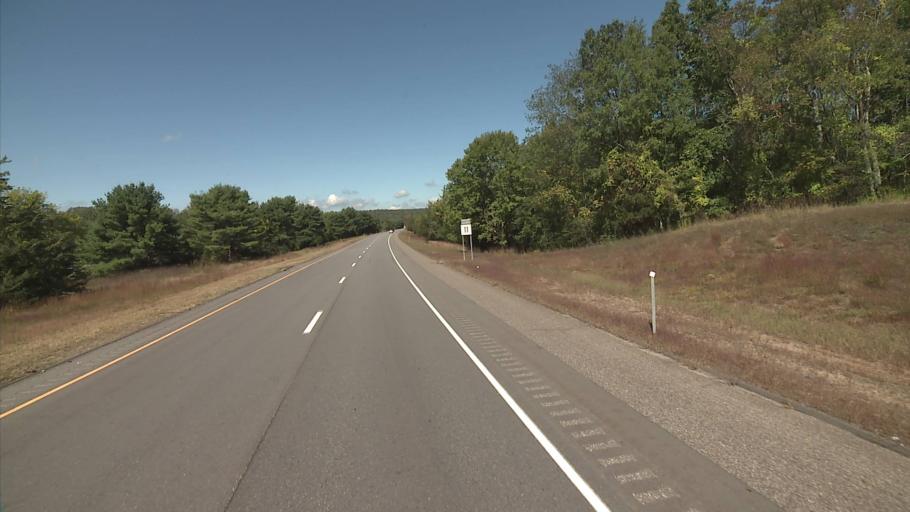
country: US
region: Connecticut
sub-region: New London County
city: Colchester
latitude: 41.4687
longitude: -72.2849
